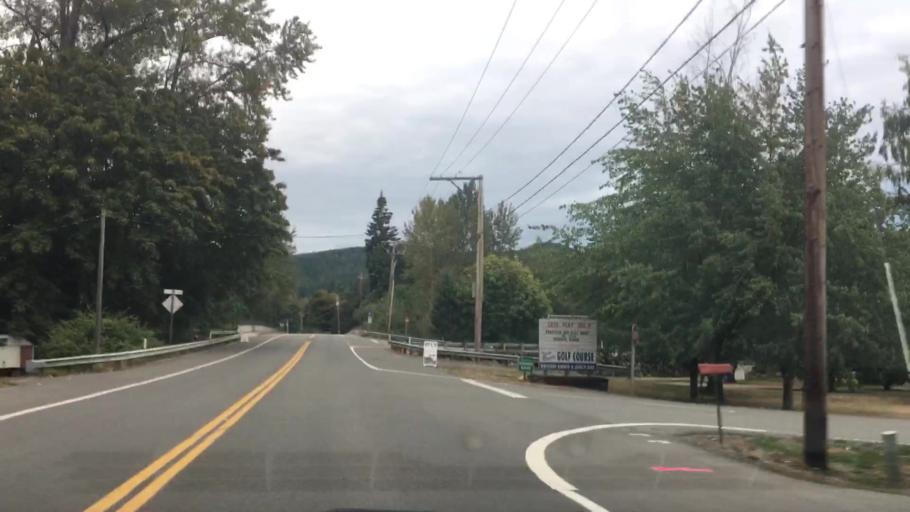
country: US
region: Washington
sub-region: King County
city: Fall City
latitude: 47.5616
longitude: -121.8923
